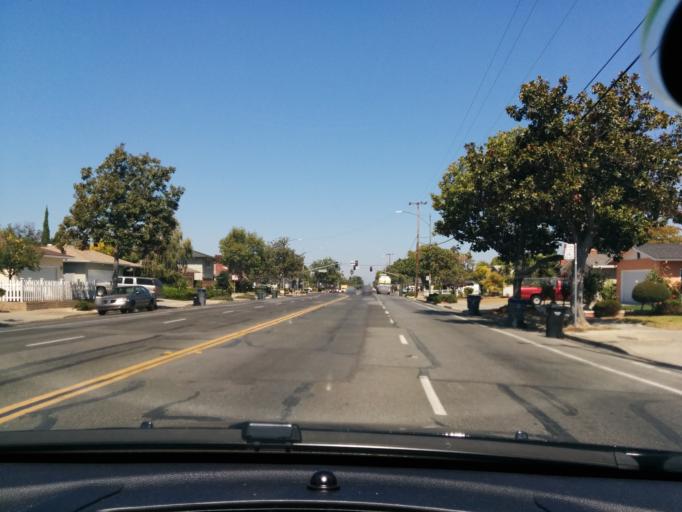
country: US
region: California
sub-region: Santa Clara County
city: Cupertino
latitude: 37.3401
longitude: -122.0143
